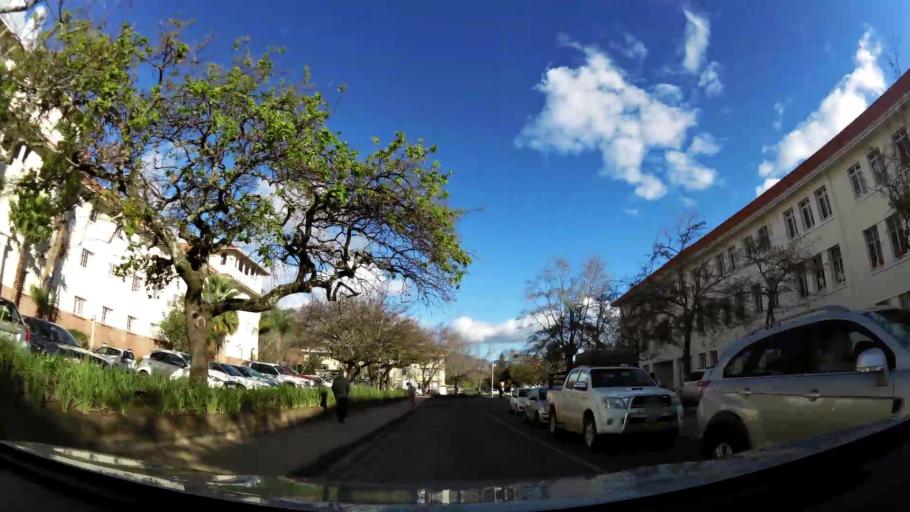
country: ZA
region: Western Cape
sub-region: Cape Winelands District Municipality
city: Stellenbosch
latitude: -33.9330
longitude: 18.8680
